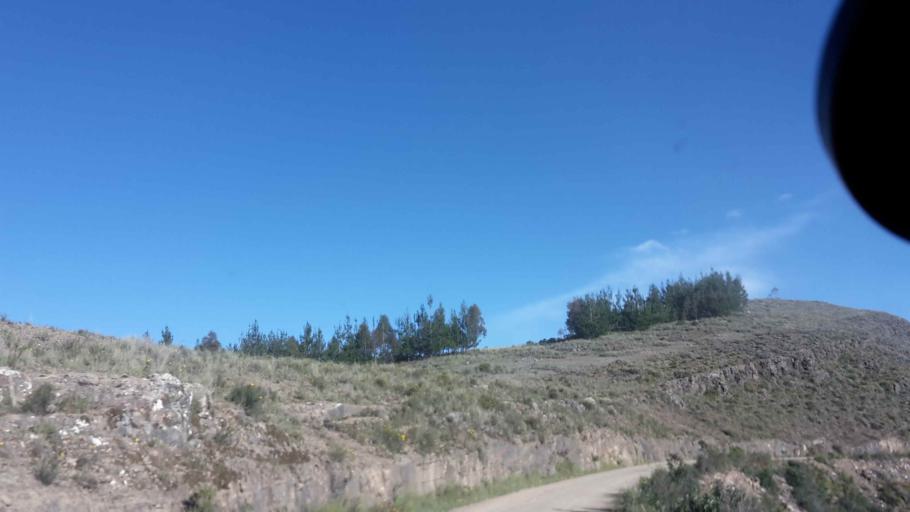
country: BO
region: Cochabamba
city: Arani
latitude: -17.7285
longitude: -65.6292
